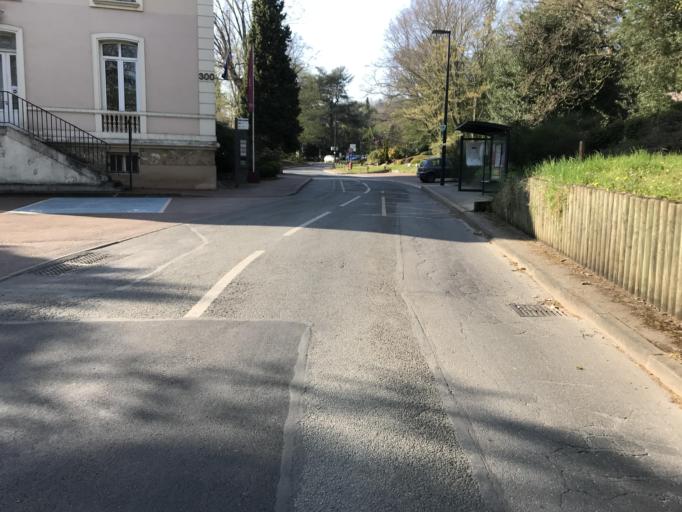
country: FR
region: Ile-de-France
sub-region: Departement de l'Essonne
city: Orsay
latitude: 48.7012
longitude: 2.1803
